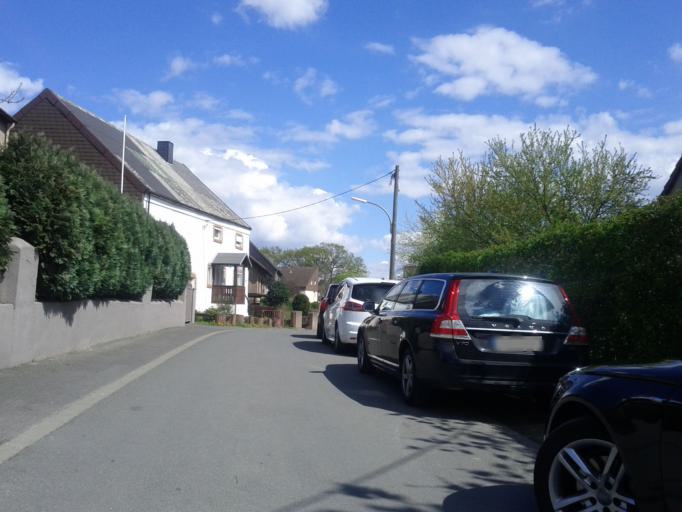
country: DE
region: North Rhine-Westphalia
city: Lanstrop
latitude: 51.5625
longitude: 7.5484
